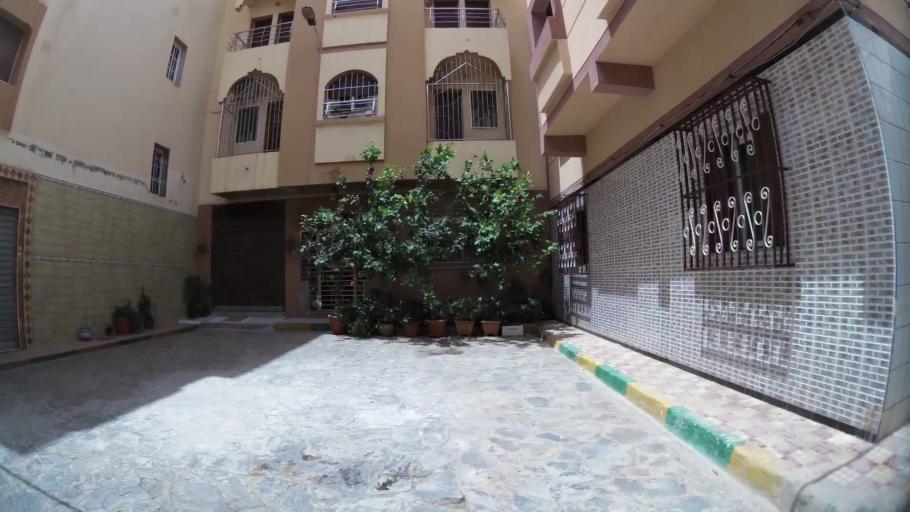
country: MA
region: Oriental
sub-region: Nador
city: Nador
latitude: 35.1697
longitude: -2.9214
